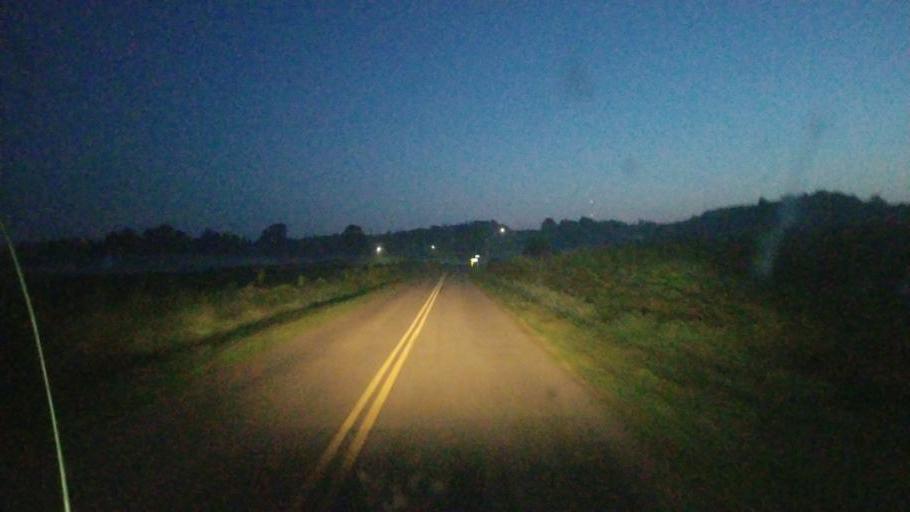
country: US
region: Ohio
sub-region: Perry County
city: Thornport
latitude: 39.9165
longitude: -82.3371
